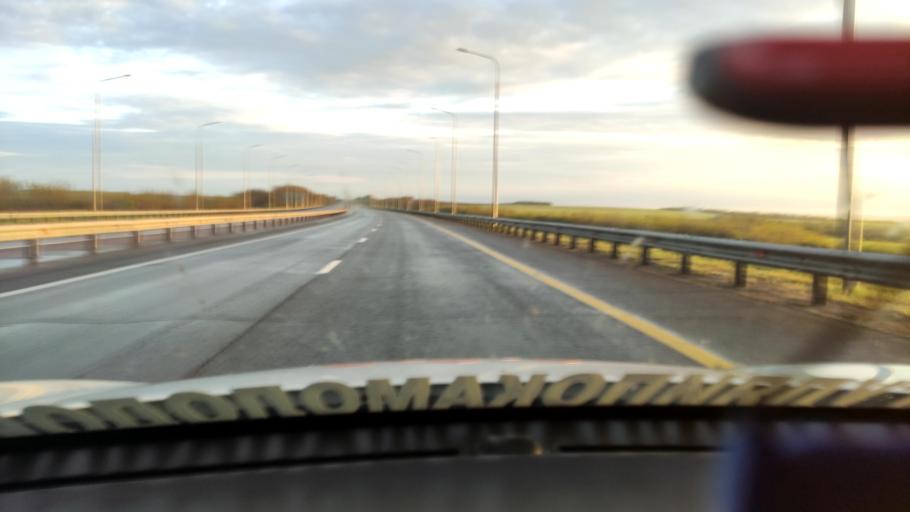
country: RU
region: Rostov
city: Millerovo
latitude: 49.2515
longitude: 40.6372
